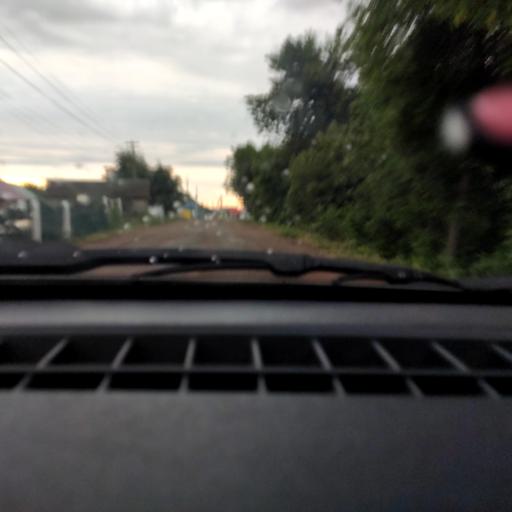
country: RU
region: Bashkortostan
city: Blagoveshchensk
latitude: 54.9292
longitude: 55.9681
